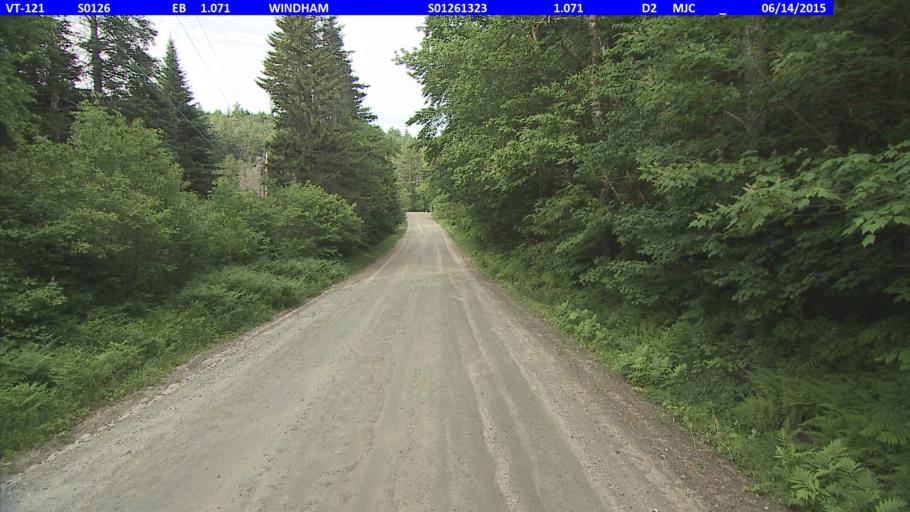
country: US
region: Vermont
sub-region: Windsor County
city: Chester
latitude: 43.1982
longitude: -72.6998
